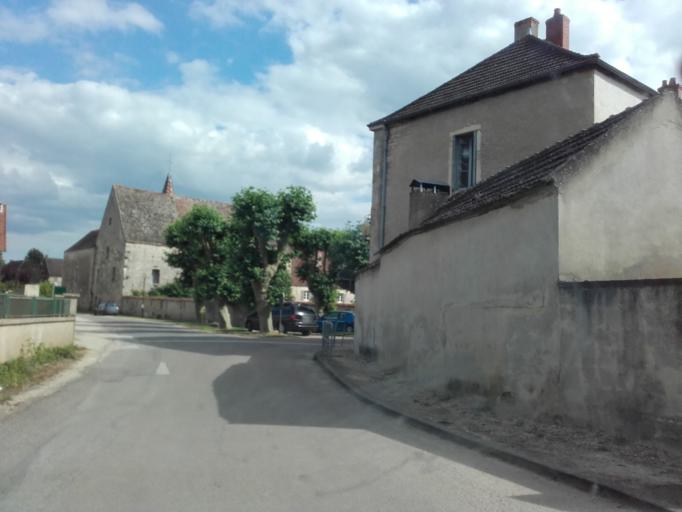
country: FR
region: Bourgogne
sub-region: Departement de Saone-et-Loire
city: Chagny
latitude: 46.9173
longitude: 4.7859
